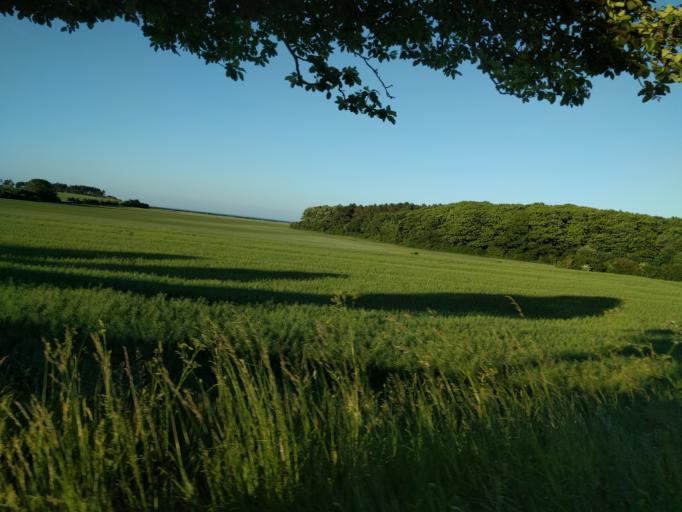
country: DK
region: South Denmark
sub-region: Kerteminde Kommune
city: Kerteminde
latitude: 55.5907
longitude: 10.6297
